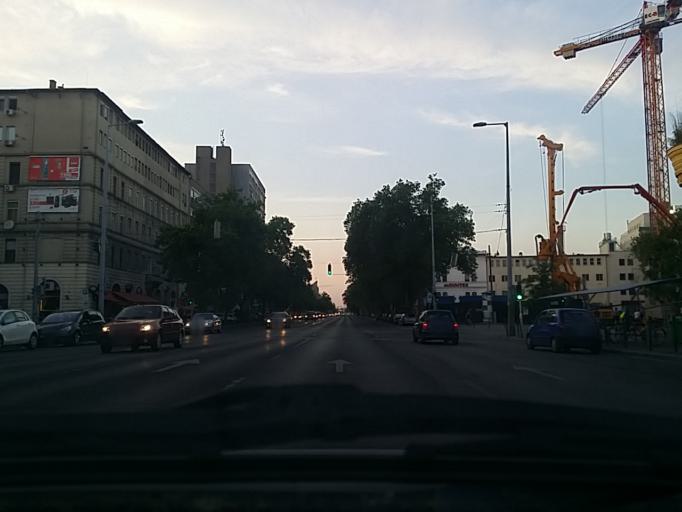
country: HU
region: Budapest
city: Budapest VI. keruelet
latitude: 47.5192
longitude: 19.0610
